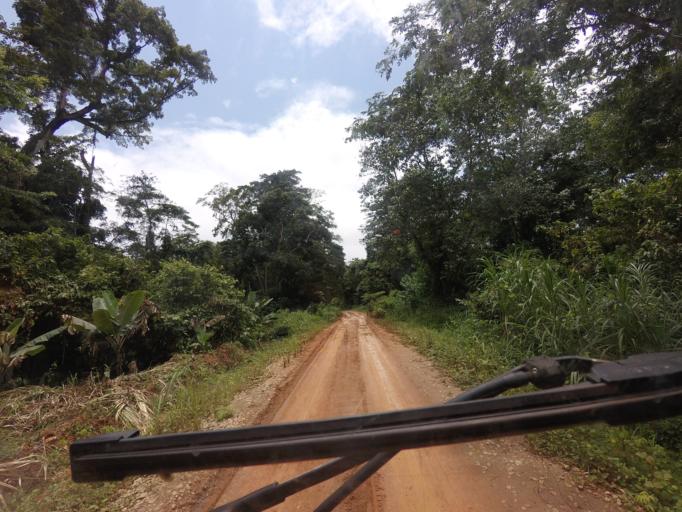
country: SL
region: Eastern Province
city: Tombodu
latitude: 8.1267
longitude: -10.6587
